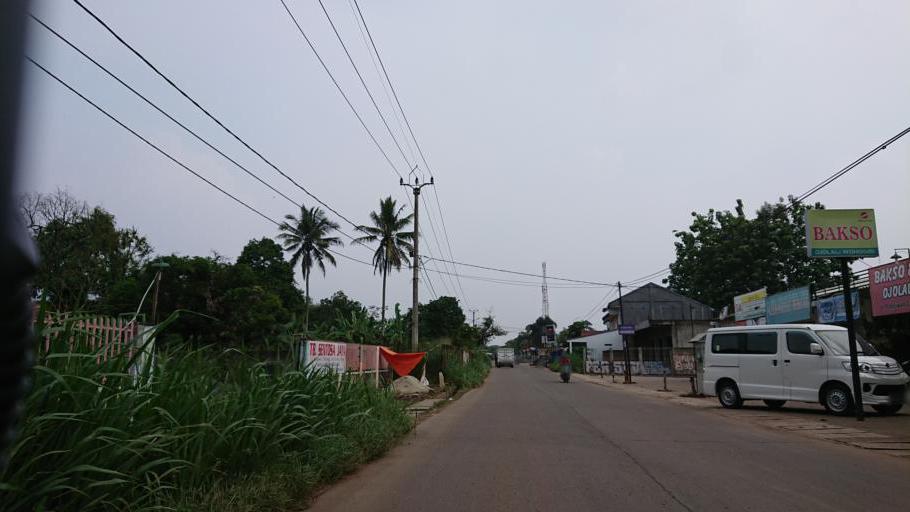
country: ID
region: West Java
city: Parung
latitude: -6.4028
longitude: 106.6912
